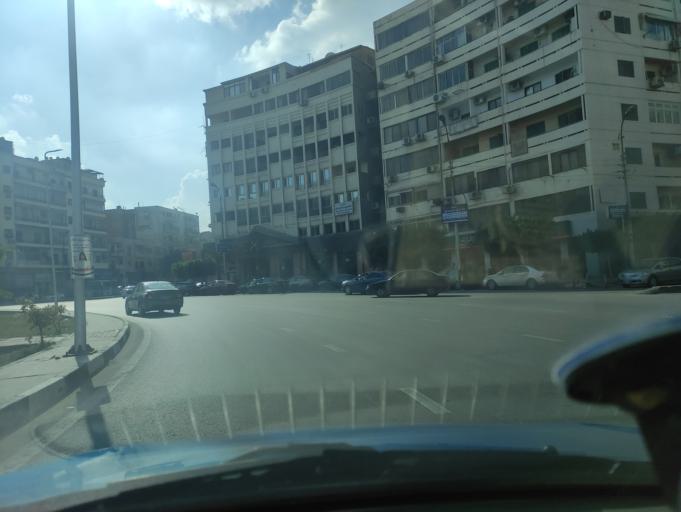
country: EG
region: Muhafazat al Qahirah
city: Cairo
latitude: 30.1007
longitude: 31.3427
